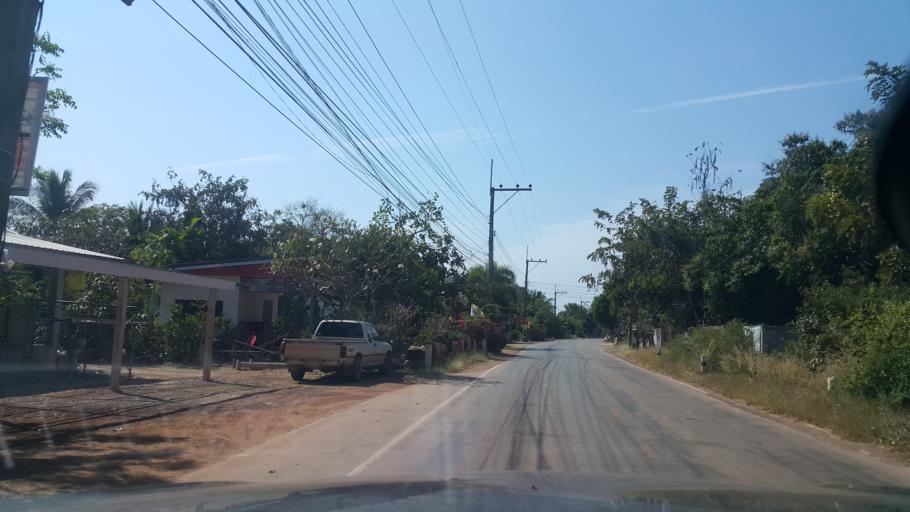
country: TH
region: Changwat Udon Thani
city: Udon Thani
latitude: 17.5065
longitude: 102.7579
